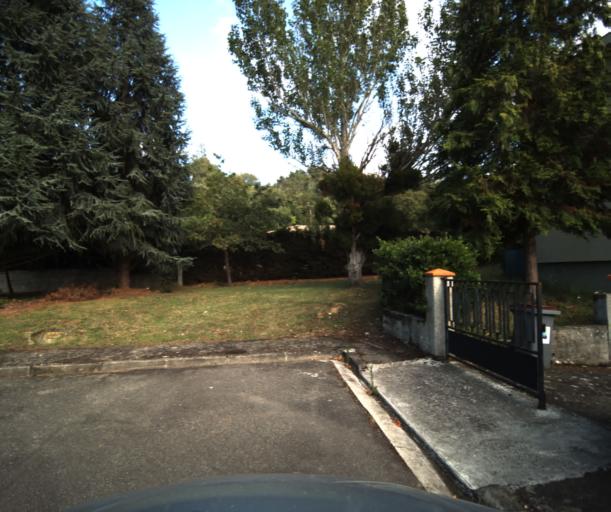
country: FR
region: Midi-Pyrenees
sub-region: Departement de la Haute-Garonne
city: Muret
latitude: 43.4548
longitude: 1.3350
